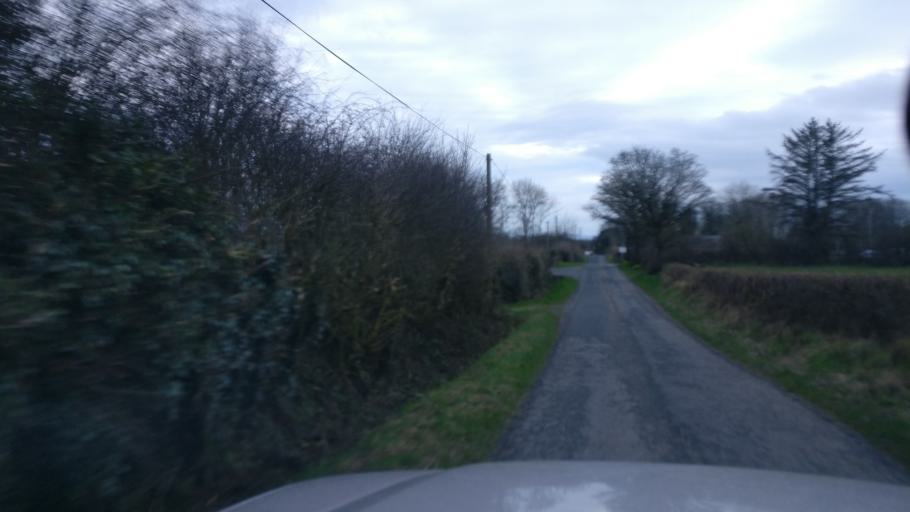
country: IE
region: Connaught
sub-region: County Galway
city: Loughrea
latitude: 53.2645
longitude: -8.5005
